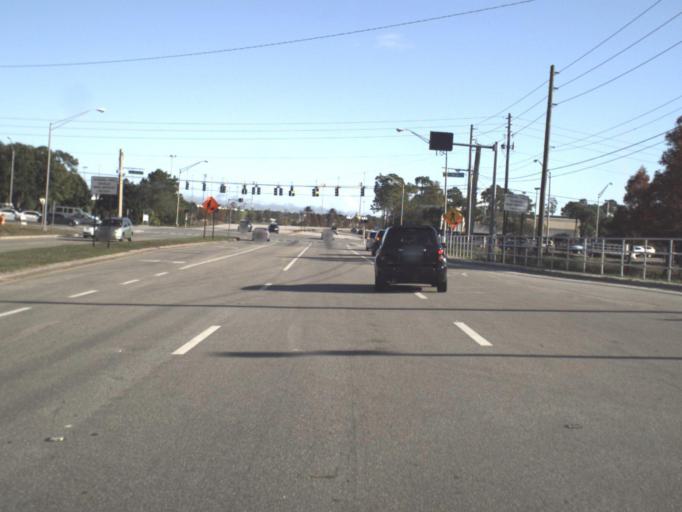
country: US
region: Florida
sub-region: Volusia County
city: Daytona Beach
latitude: 29.1826
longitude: -81.0804
